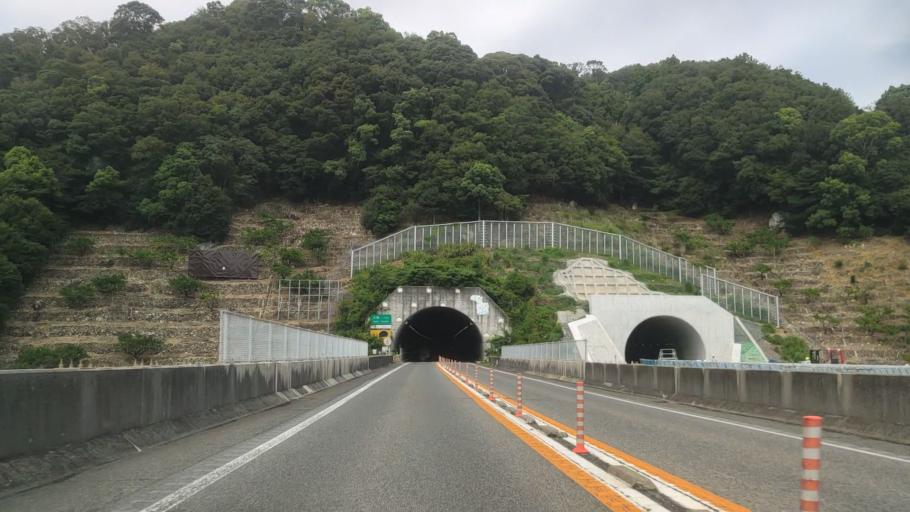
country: JP
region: Wakayama
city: Gobo
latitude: 33.9985
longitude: 135.1961
